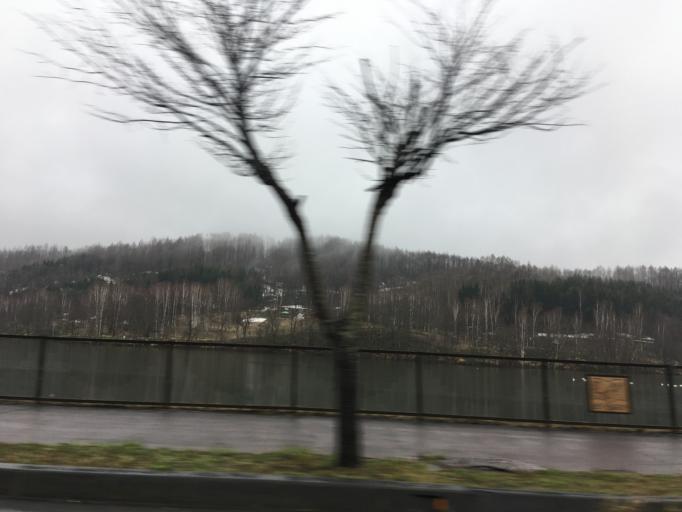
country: JP
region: Hokkaido
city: Nayoro
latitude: 44.0965
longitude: 142.4356
